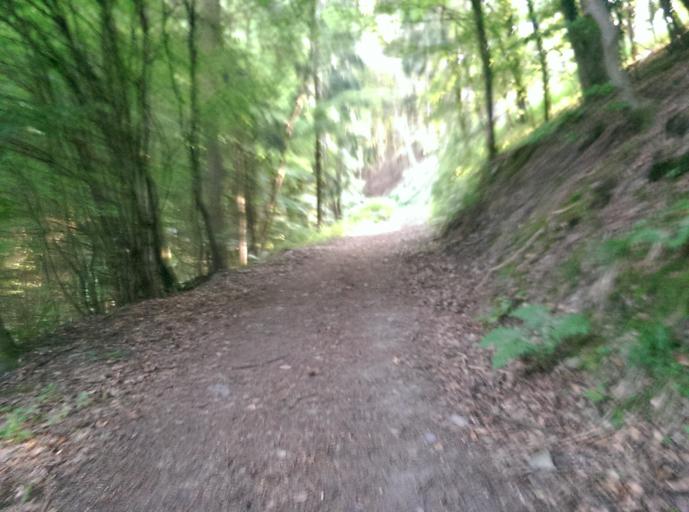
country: DE
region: Rheinland-Pfalz
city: Melsbach
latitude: 50.4904
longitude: 7.4609
